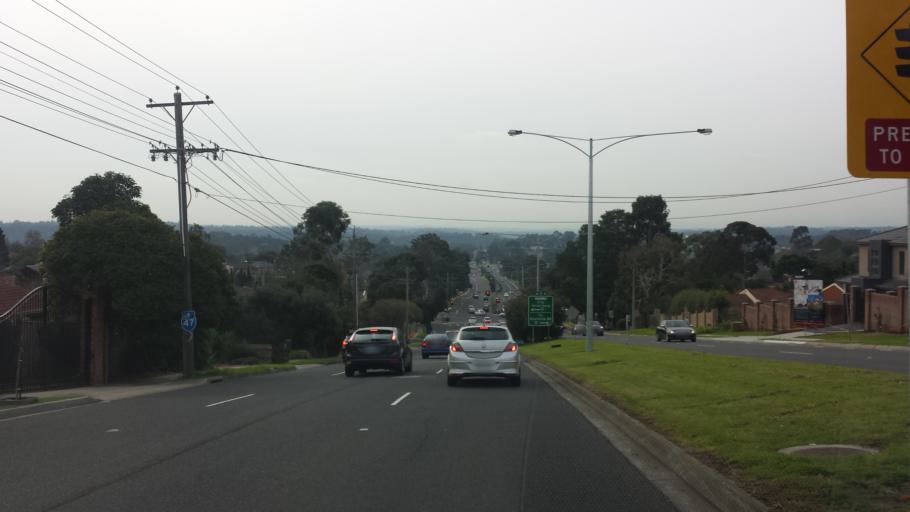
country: AU
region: Victoria
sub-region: Manningham
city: Templestowe Lower
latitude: -37.7616
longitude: 145.1335
